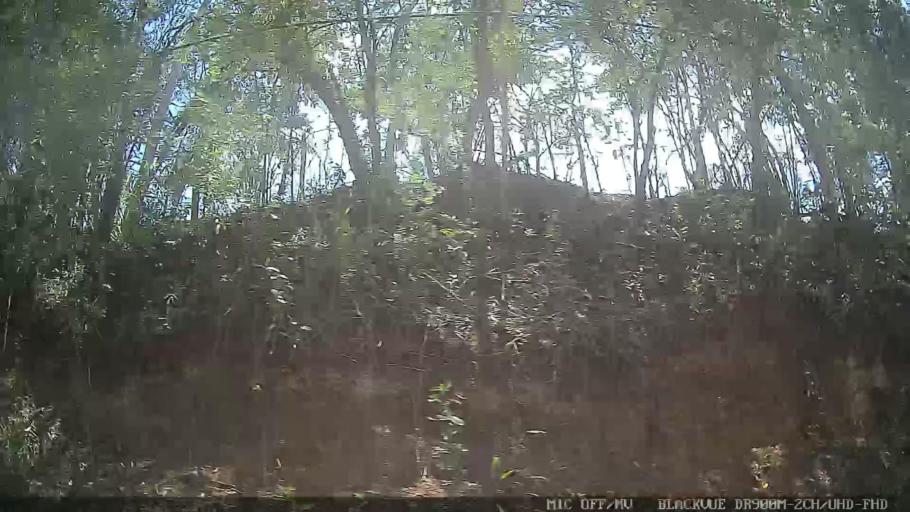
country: BR
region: Sao Paulo
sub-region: Laranjal Paulista
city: Laranjal Paulista
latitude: -23.0280
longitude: -47.8422
